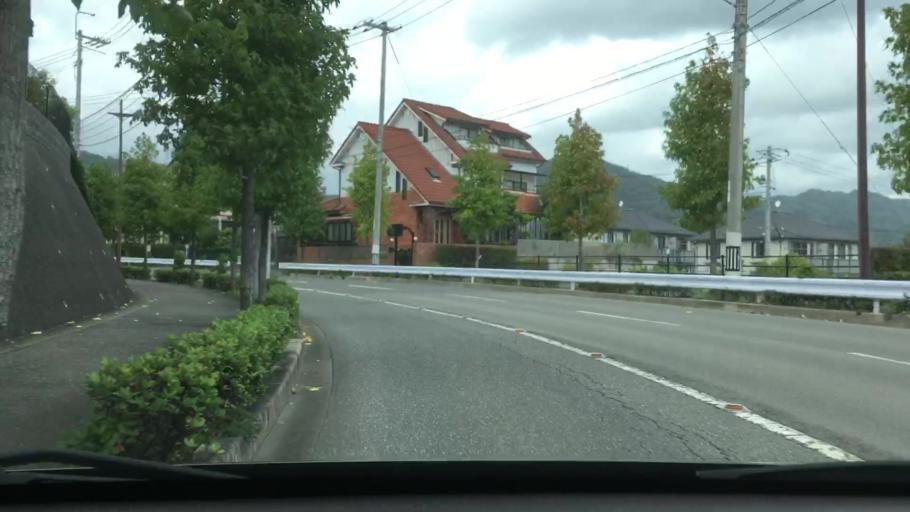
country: JP
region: Hiroshima
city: Hiroshima-shi
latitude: 34.4006
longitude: 132.4176
